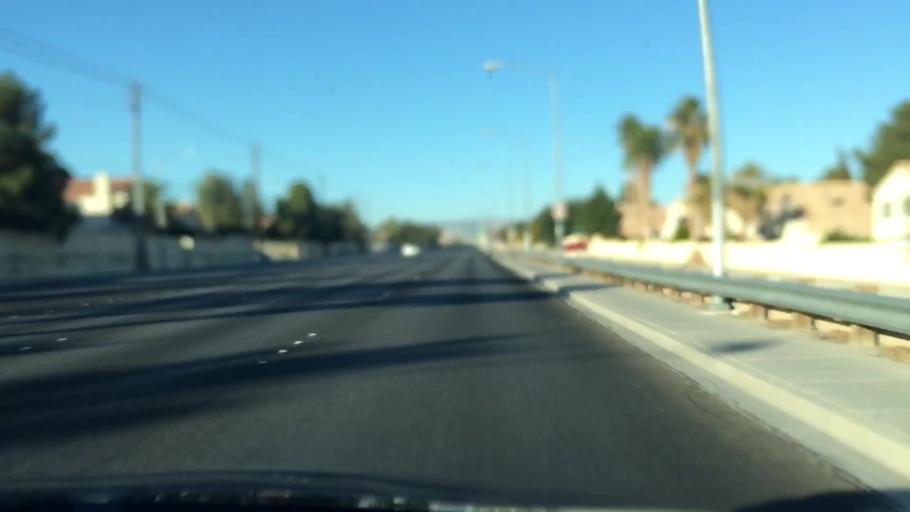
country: US
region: Nevada
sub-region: Clark County
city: Paradise
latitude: 36.0427
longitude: -115.1427
